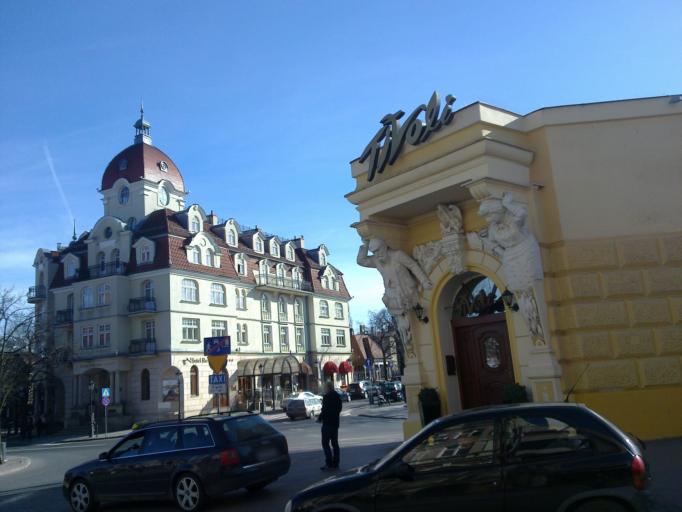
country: PL
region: Pomeranian Voivodeship
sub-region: Sopot
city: Sopot
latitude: 54.4432
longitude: 18.5622
